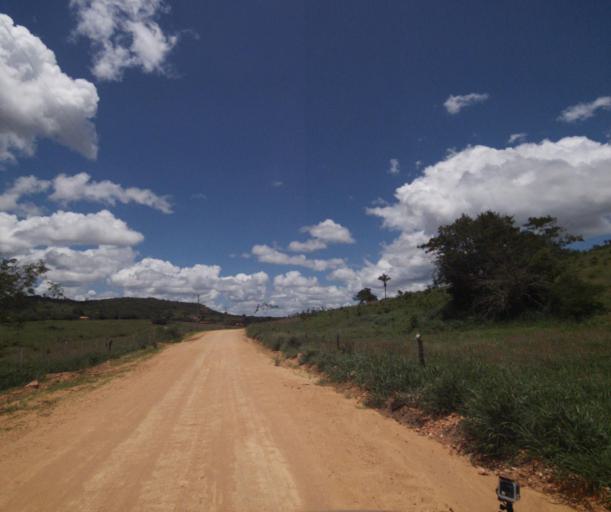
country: BR
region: Bahia
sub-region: Pocoes
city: Pocoes
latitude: -14.3870
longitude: -40.4215
